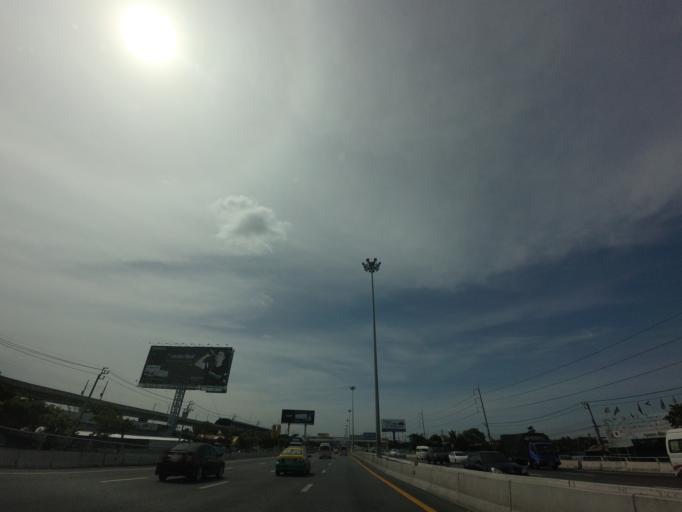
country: TH
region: Bangkok
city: Saphan Sung
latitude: 13.7334
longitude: 100.6946
